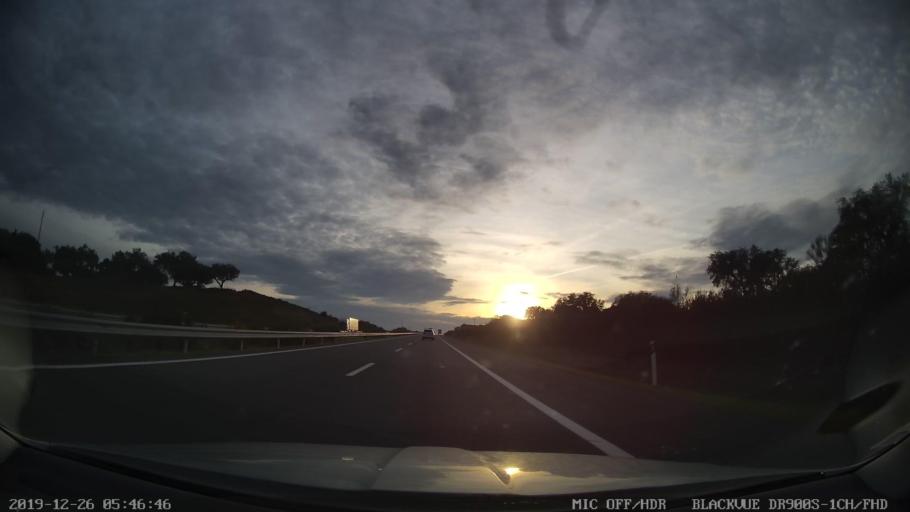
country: PT
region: Evora
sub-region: Estremoz
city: Estremoz
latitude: 38.7358
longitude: -7.7621
